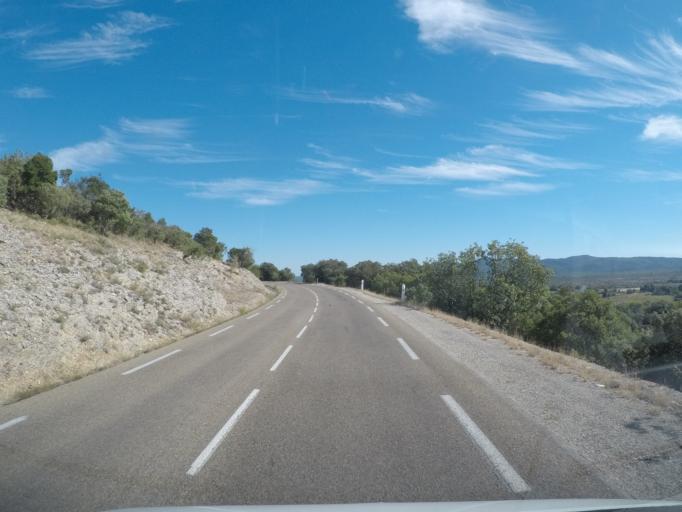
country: FR
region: Languedoc-Roussillon
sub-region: Departement du Gard
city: Saint-Hippolyte-du-Fort
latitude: 43.9604
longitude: 3.9039
